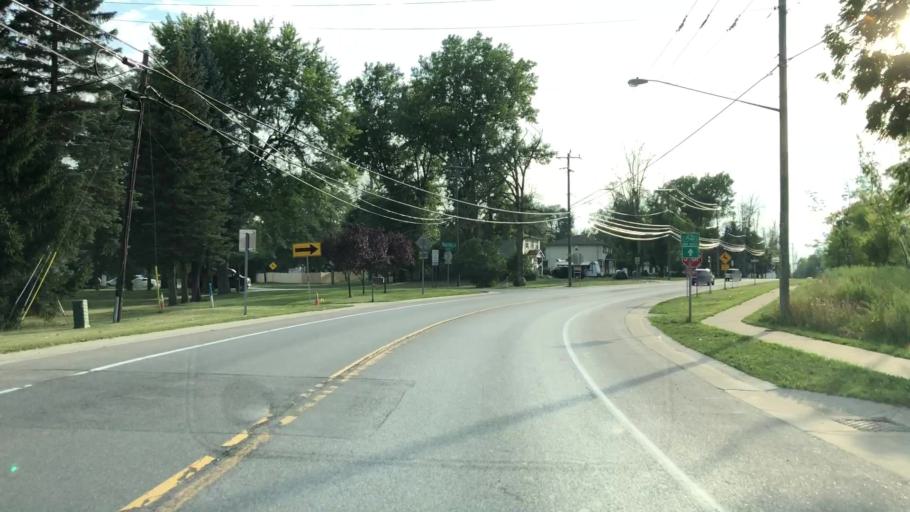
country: US
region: New York
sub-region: Erie County
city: Cheektowaga
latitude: 42.8928
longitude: -78.7413
